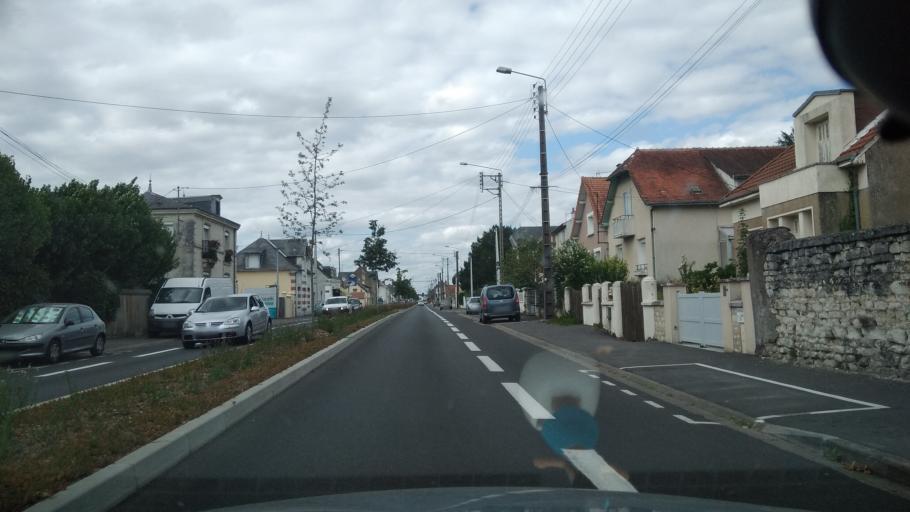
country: FR
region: Poitou-Charentes
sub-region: Departement de la Vienne
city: Antran
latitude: 46.8285
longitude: 0.5455
